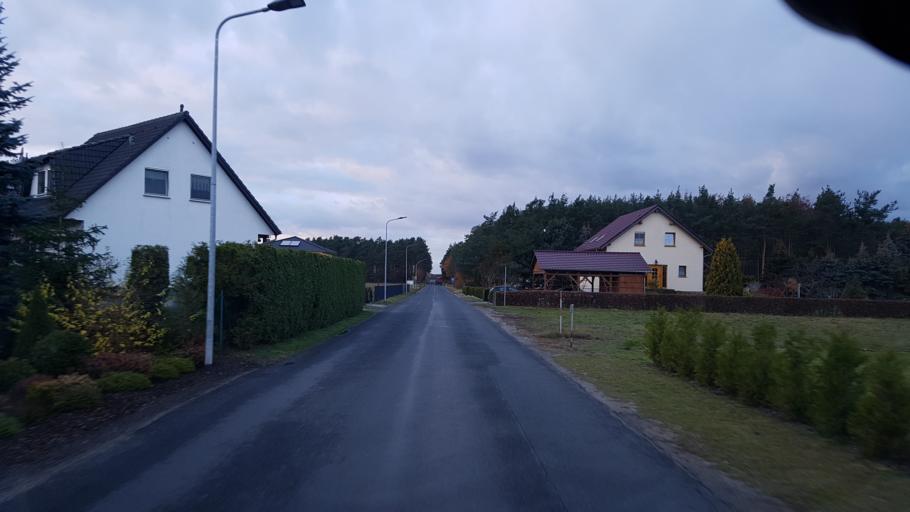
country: DE
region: Brandenburg
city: Tettau
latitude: 51.4167
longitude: 13.7652
